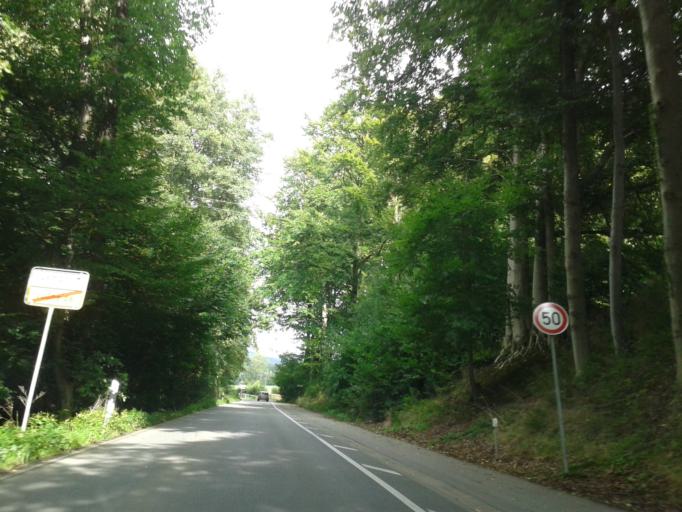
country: DE
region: North Rhine-Westphalia
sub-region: Regierungsbezirk Detmold
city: Dorentrup
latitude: 52.0118
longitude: 8.9606
